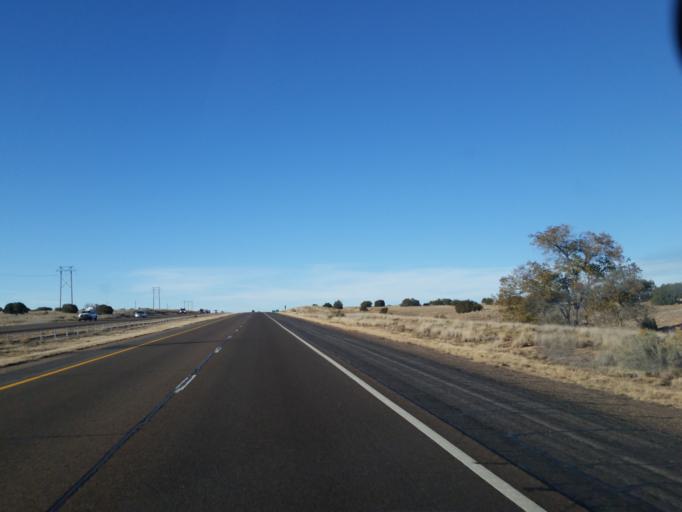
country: US
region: New Mexico
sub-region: Sandoval County
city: Santo Domingo Pueblo
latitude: 35.4757
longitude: -106.2918
